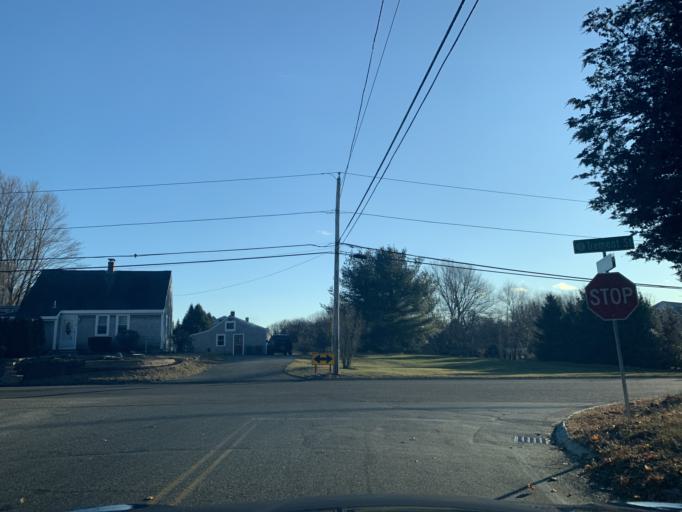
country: US
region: Massachusetts
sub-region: Bristol County
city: Norton
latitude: 41.9034
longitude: -71.2022
